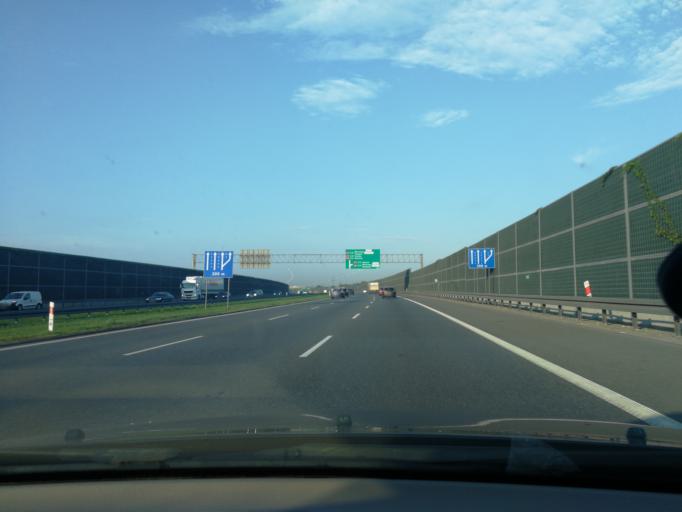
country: PL
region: Masovian Voivodeship
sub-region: Powiat pruszkowski
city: Pruszkow
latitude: 52.1930
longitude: 20.8161
